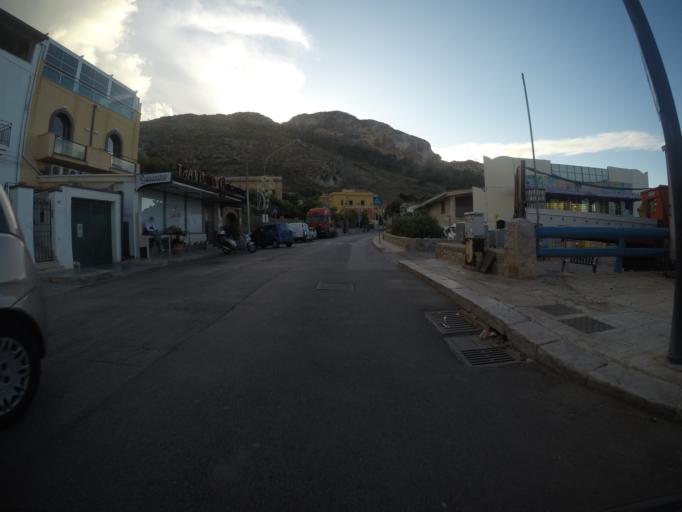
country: IT
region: Sicily
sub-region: Palermo
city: Isola delle Femmine
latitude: 38.1978
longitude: 13.2736
